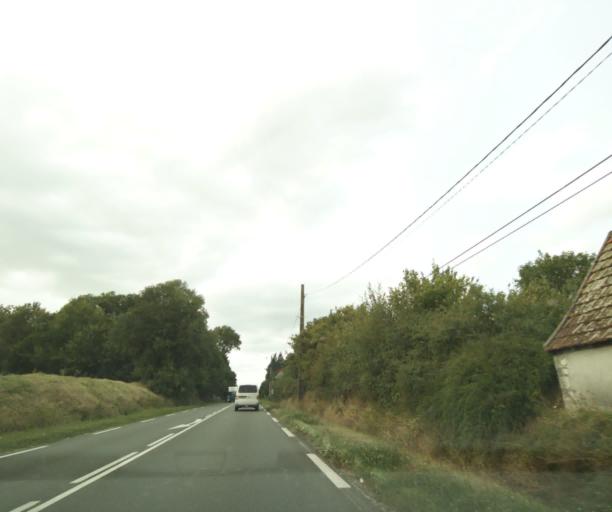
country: FR
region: Centre
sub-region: Departement d'Indre-et-Loire
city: Loches
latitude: 47.1570
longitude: 0.9944
